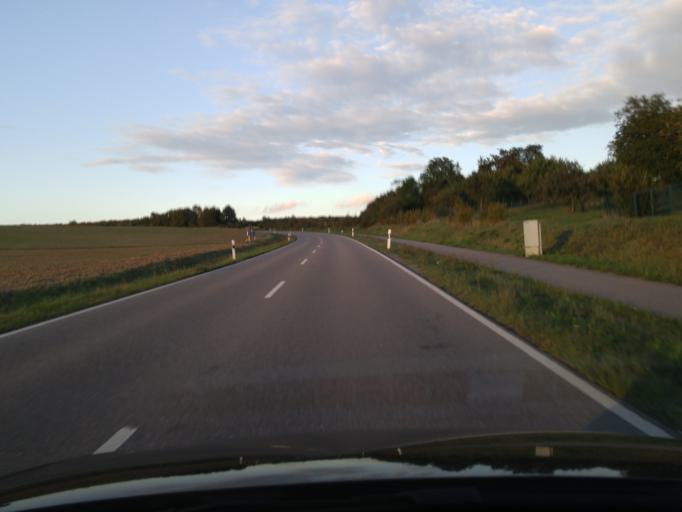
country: DE
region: Baden-Wuerttemberg
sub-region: Regierungsbezirk Stuttgart
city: Bad Rappenau
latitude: 49.2193
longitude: 9.1051
